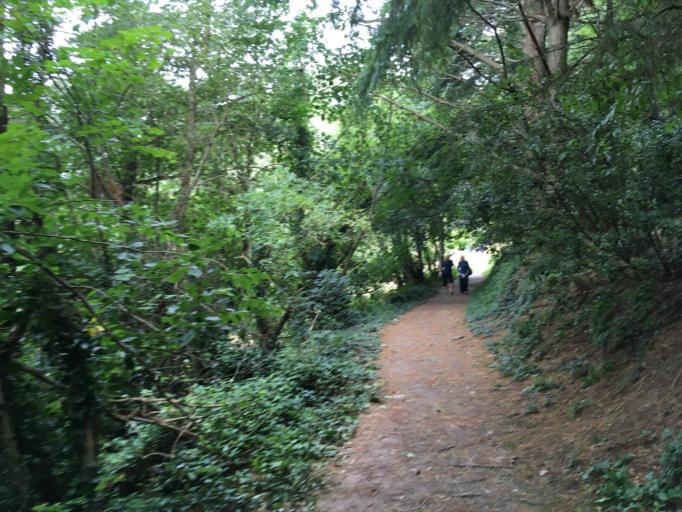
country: GB
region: England
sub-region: Devon
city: Dartmouth
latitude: 50.3462
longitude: -3.5301
